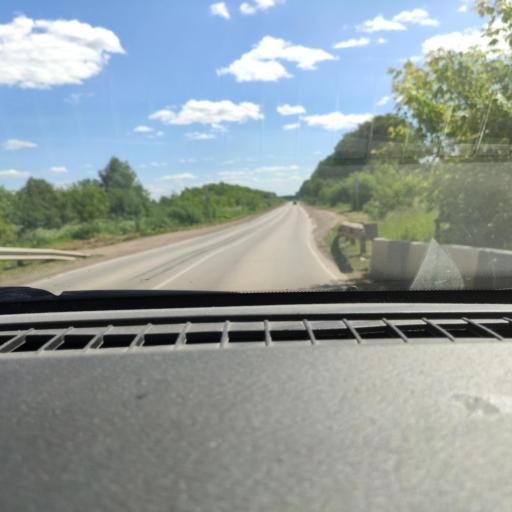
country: RU
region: Perm
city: Chaykovskaya
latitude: 58.1110
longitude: 55.5860
